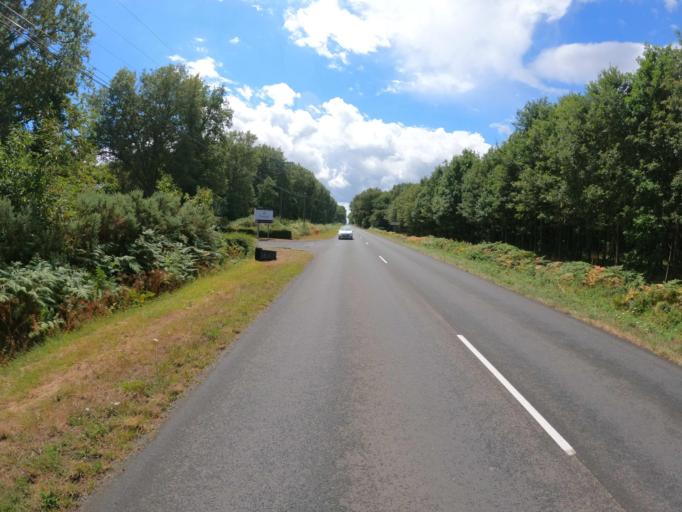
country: FR
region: Pays de la Loire
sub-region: Departement de Maine-et-Loire
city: Feneu
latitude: 47.5848
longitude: -0.5910
